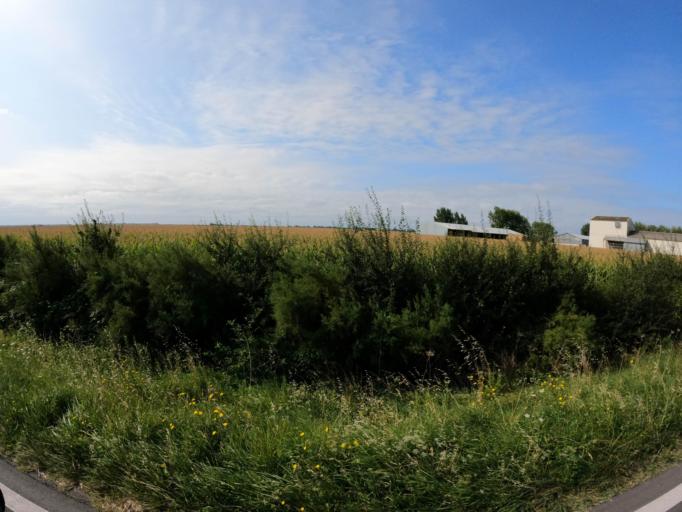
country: FR
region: Pays de la Loire
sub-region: Departement de la Vendee
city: Triaize
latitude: 46.3379
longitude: -1.2799
